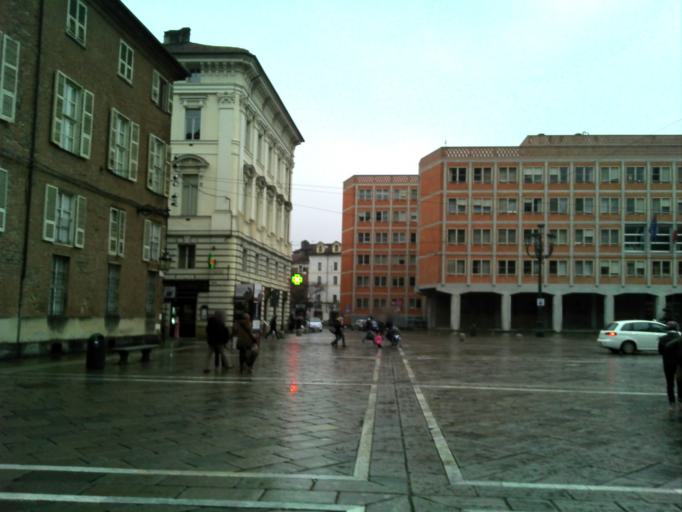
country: IT
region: Piedmont
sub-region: Provincia di Torino
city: Turin
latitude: 45.0731
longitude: 7.6851
